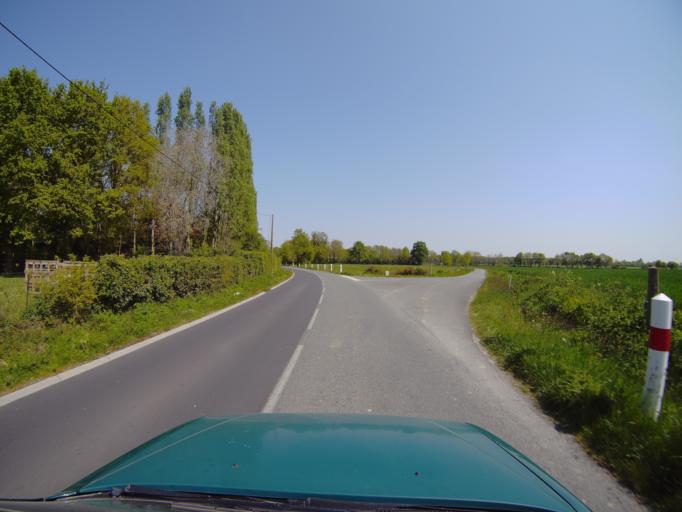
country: FR
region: Pays de la Loire
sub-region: Departement de la Vendee
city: Bouffere
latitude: 46.9413
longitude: -1.3681
